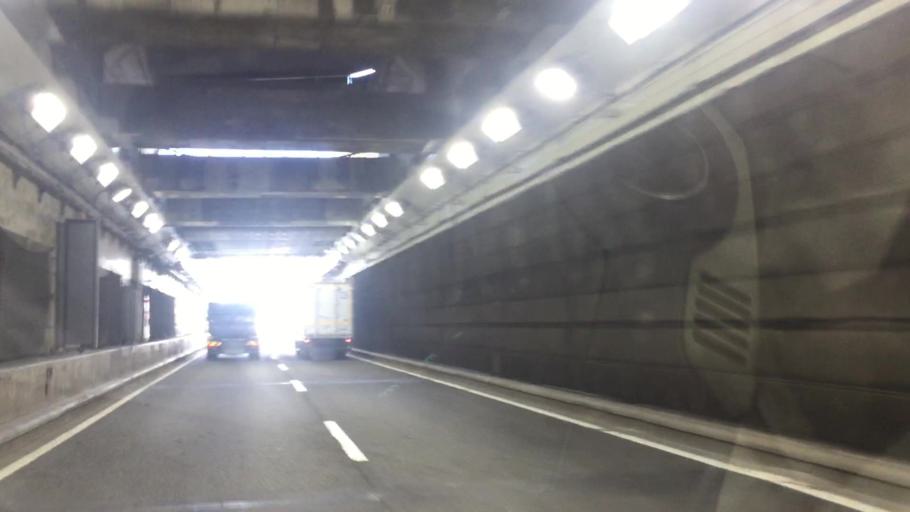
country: JP
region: Kanagawa
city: Yokohama
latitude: 35.4700
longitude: 139.6131
